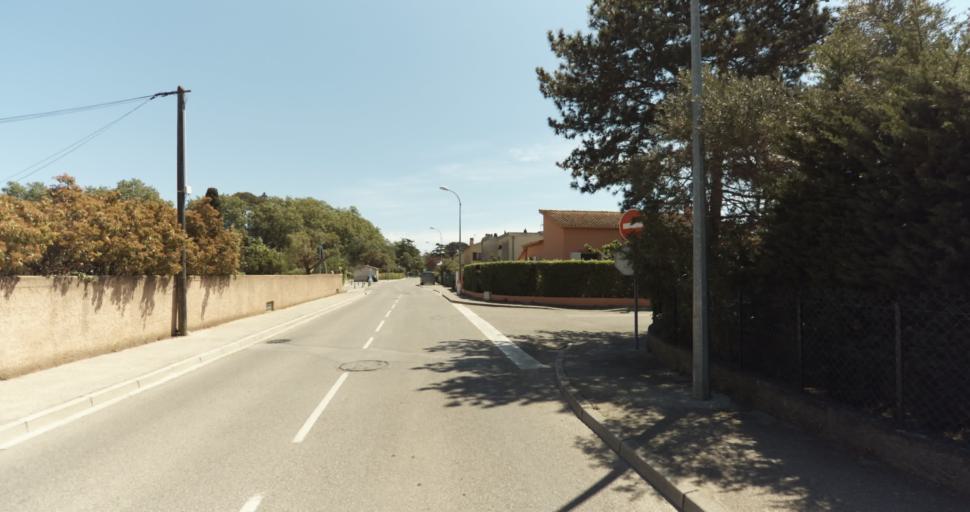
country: FR
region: Provence-Alpes-Cote d'Azur
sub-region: Departement du Var
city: La Crau
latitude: 43.1493
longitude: 6.0804
